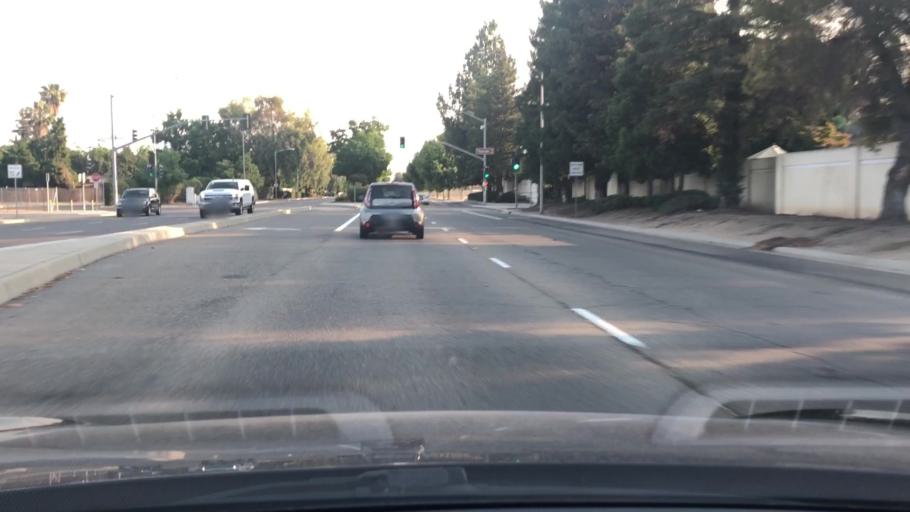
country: US
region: California
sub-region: Fresno County
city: Clovis
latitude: 36.8257
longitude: -119.7294
